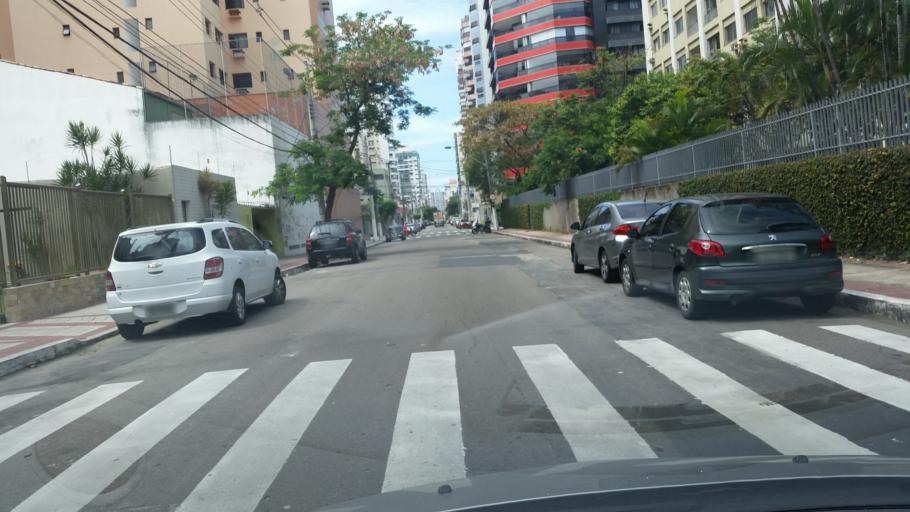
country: BR
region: Espirito Santo
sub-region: Vila Velha
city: Vila Velha
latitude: -20.3423
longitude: -40.2862
